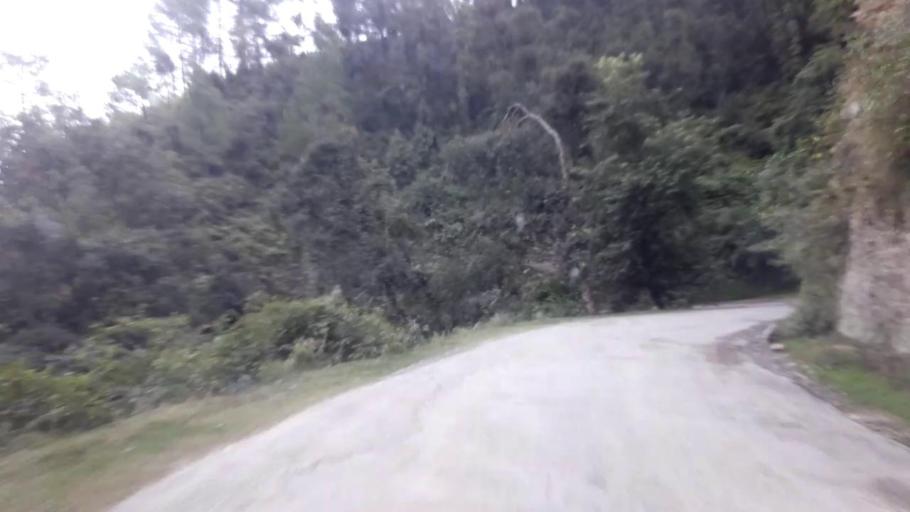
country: IN
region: Himachal Pradesh
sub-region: Shimla
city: Shimla
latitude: 31.0606
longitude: 77.1487
